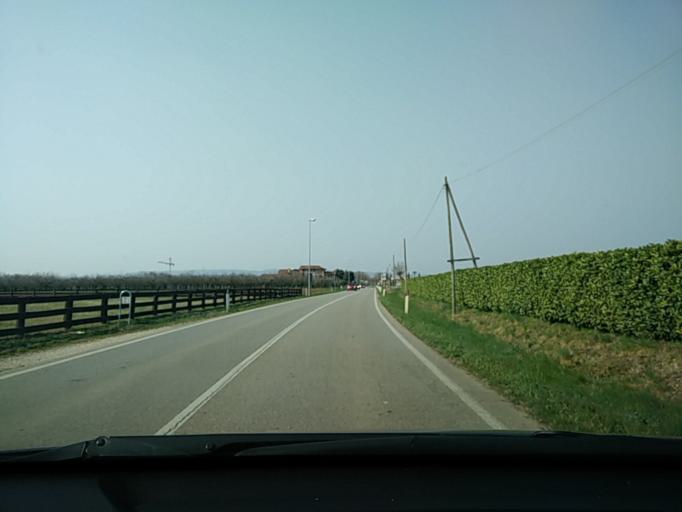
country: IT
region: Veneto
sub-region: Provincia di Treviso
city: Camalo
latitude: 45.7421
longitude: 12.1765
